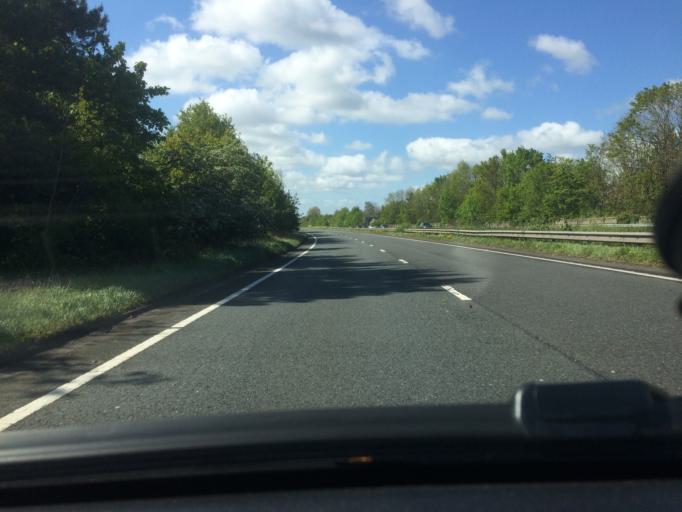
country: GB
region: England
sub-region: Cheshire West and Chester
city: Hoole
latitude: 53.1788
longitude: -2.8561
